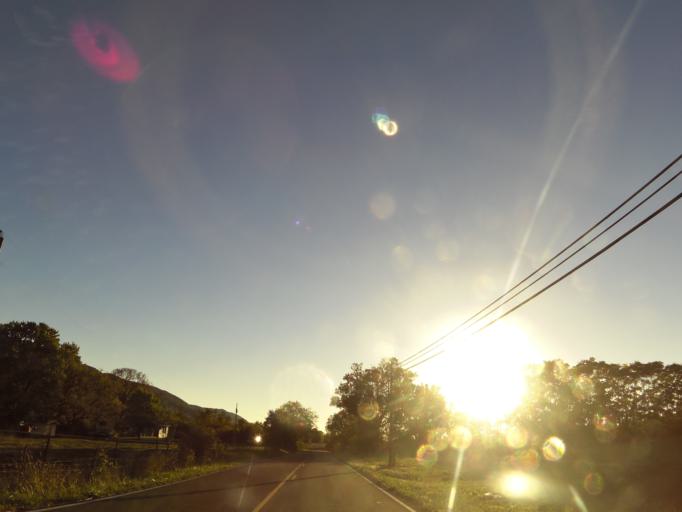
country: US
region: Tennessee
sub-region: Grainger County
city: Rutledge
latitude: 36.3033
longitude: -83.5695
